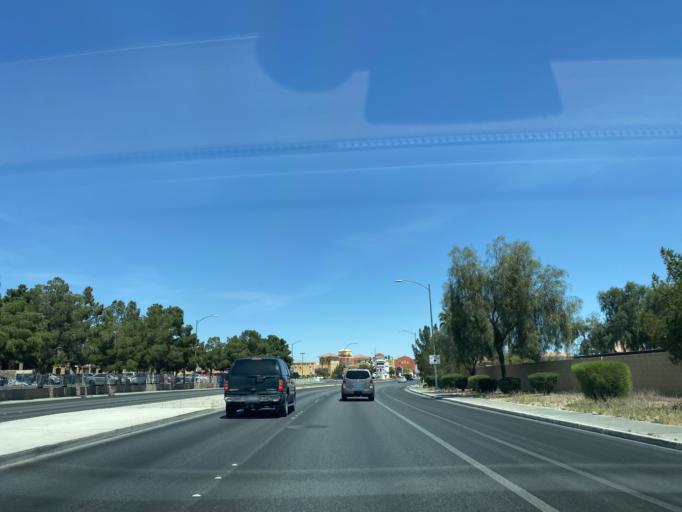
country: US
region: Nevada
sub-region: Clark County
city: Las Vegas
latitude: 36.1993
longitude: -115.1987
